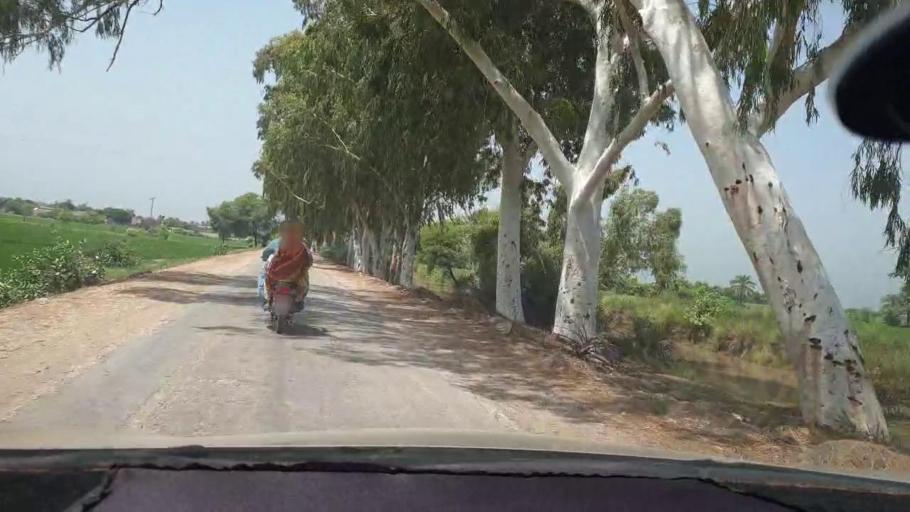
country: PK
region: Sindh
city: Kambar
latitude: 27.6340
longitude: 67.9862
